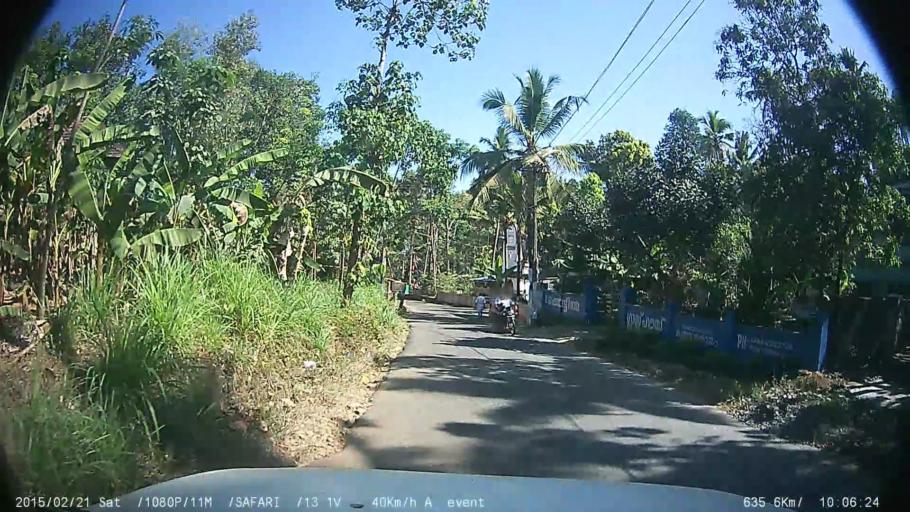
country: IN
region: Kerala
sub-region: Ernakulam
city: Piravam
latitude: 9.8668
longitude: 76.6086
